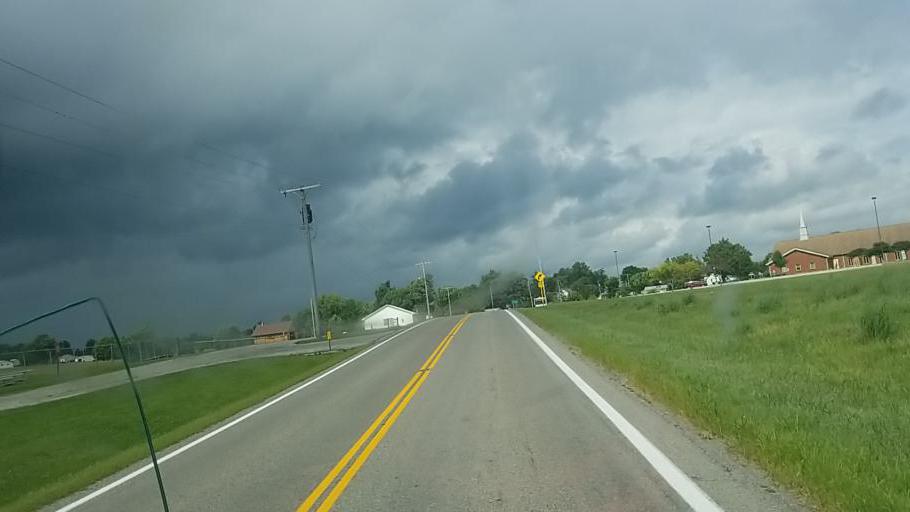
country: US
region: Ohio
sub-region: Champaign County
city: North Lewisburg
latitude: 40.2896
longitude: -83.5846
